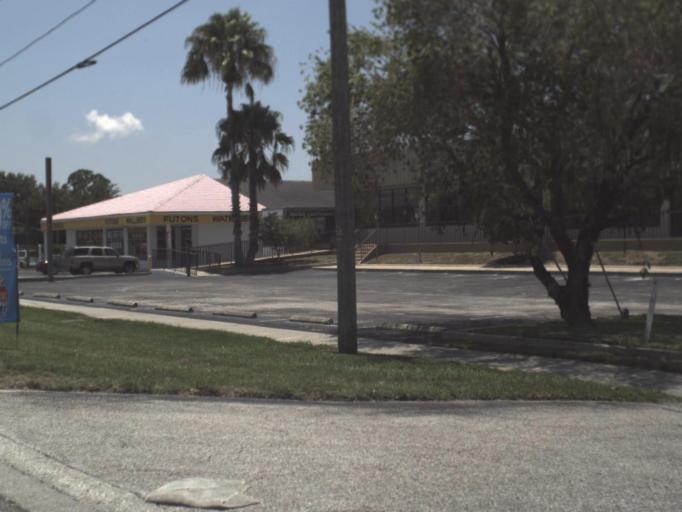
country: US
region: Florida
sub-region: Pasco County
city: New Port Richey
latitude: 28.2565
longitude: -82.7279
